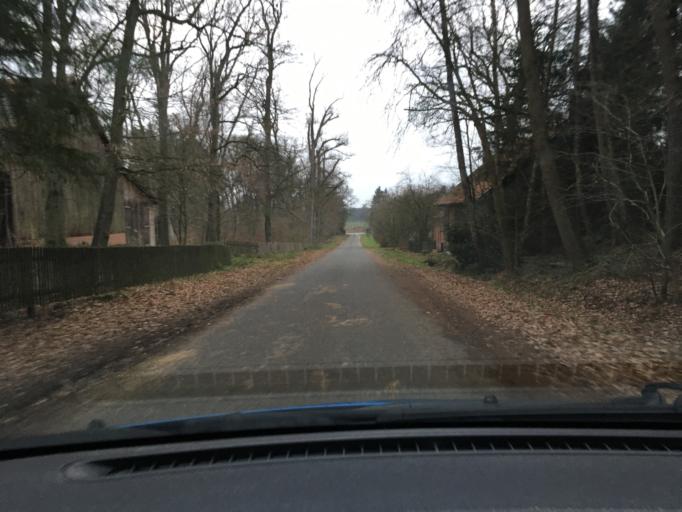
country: DE
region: Lower Saxony
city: Walsrode
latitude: 52.8329
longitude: 9.5704
